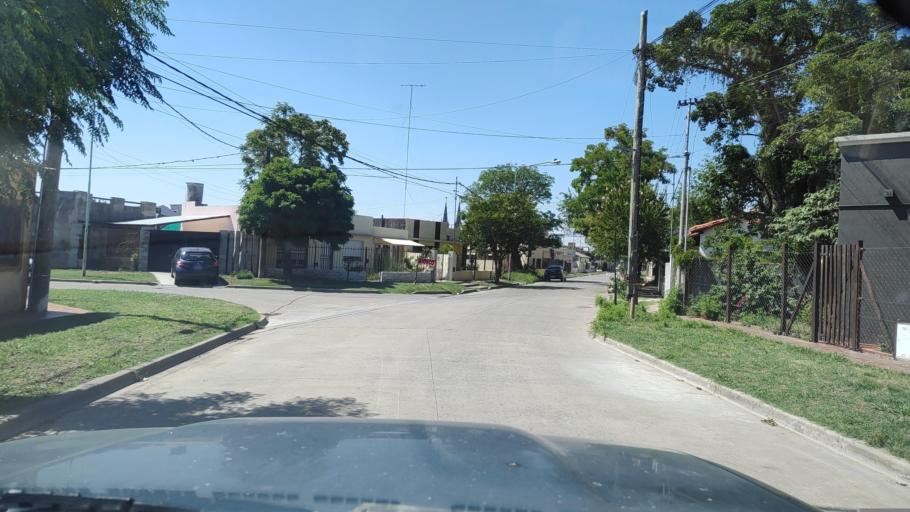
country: AR
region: Buenos Aires
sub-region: Partido de Lujan
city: Lujan
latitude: -34.5735
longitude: -59.1216
